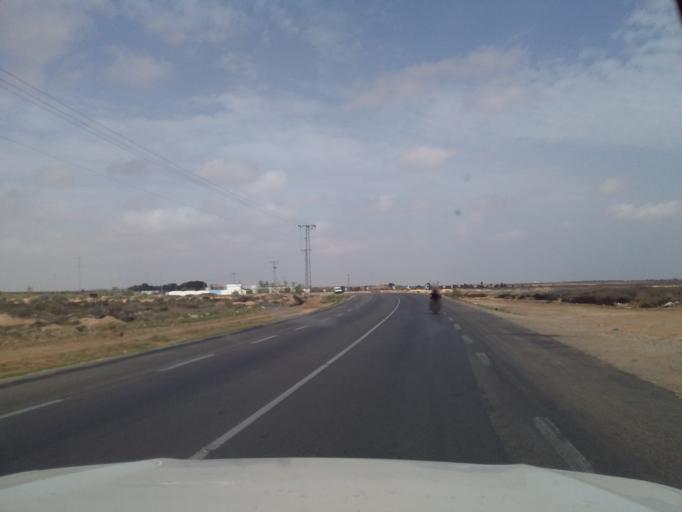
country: TN
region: Qabis
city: Gabes
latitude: 33.6388
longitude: 10.2827
